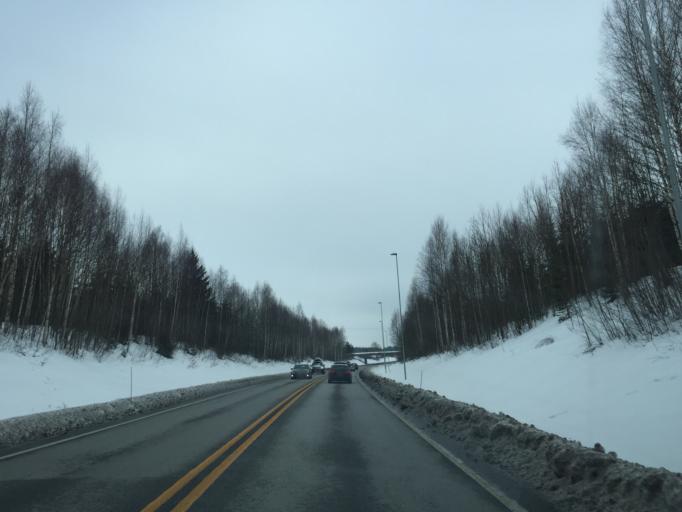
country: NO
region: Hedmark
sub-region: Loten
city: Loten
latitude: 60.7935
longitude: 11.2950
